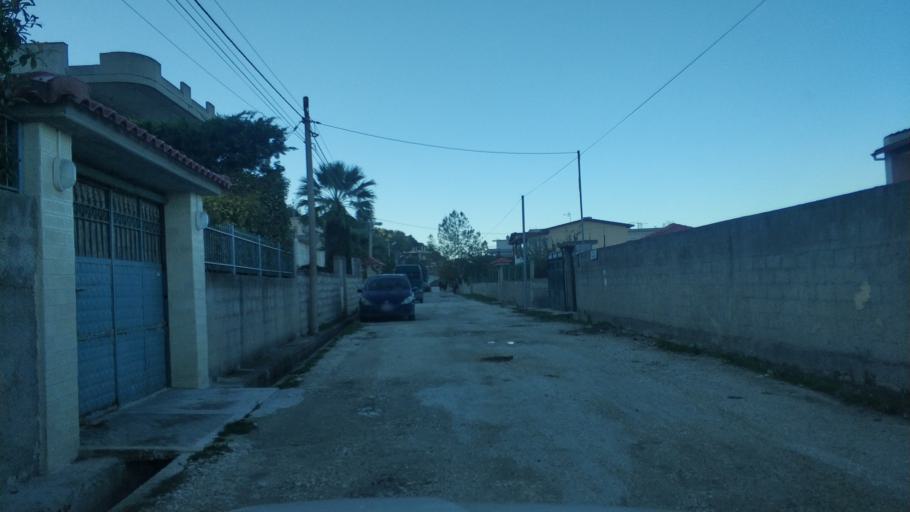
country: AL
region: Vlore
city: Vlore
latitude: 40.5121
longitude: 19.4203
